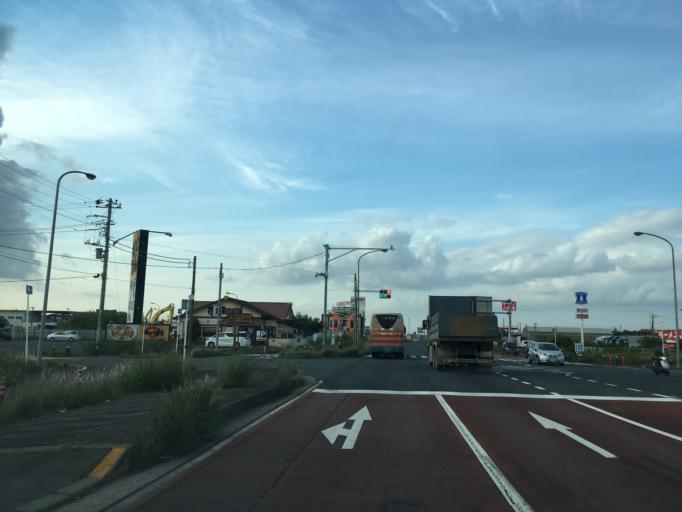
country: JP
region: Chiba
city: Kisarazu
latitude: 35.3943
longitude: 139.9411
